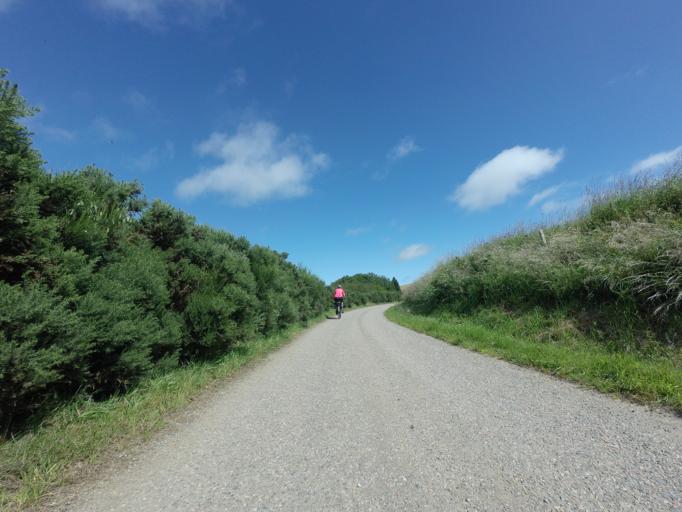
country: GB
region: Scotland
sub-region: Aberdeenshire
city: Banff
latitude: 57.5997
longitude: -2.5119
